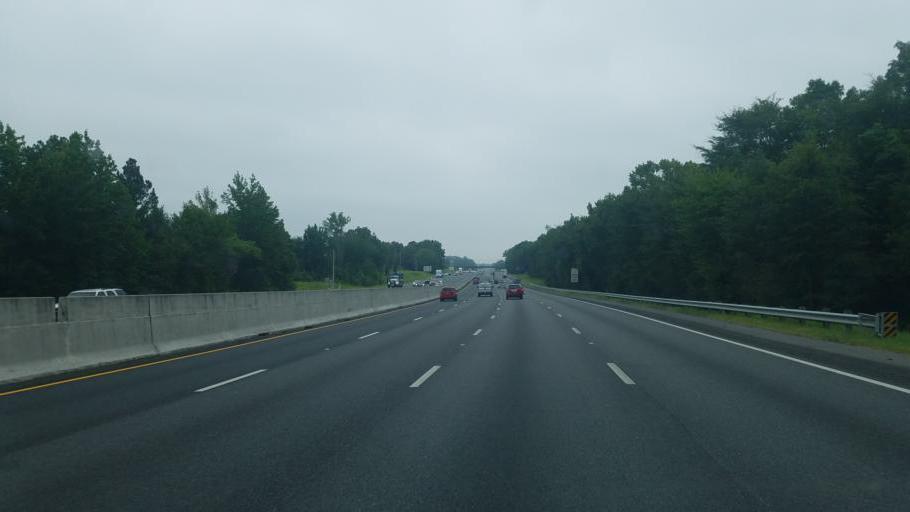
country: US
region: South Carolina
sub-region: York County
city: Fort Mill
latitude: 35.0360
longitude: -80.9607
